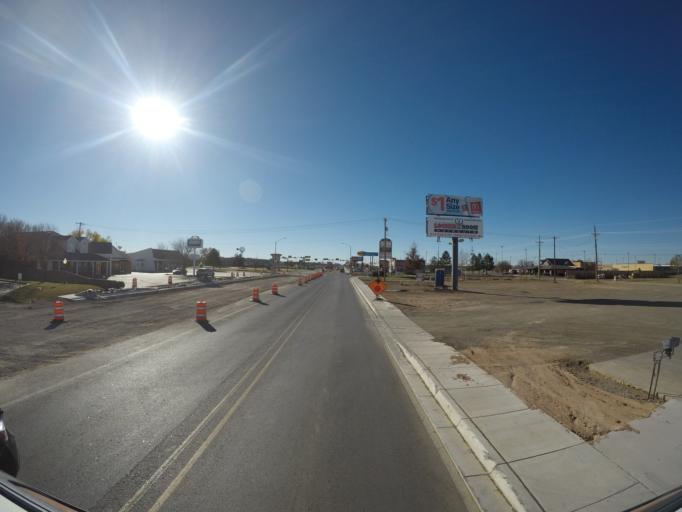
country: US
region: New Mexico
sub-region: Curry County
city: Clovis
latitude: 34.4403
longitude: -103.1965
